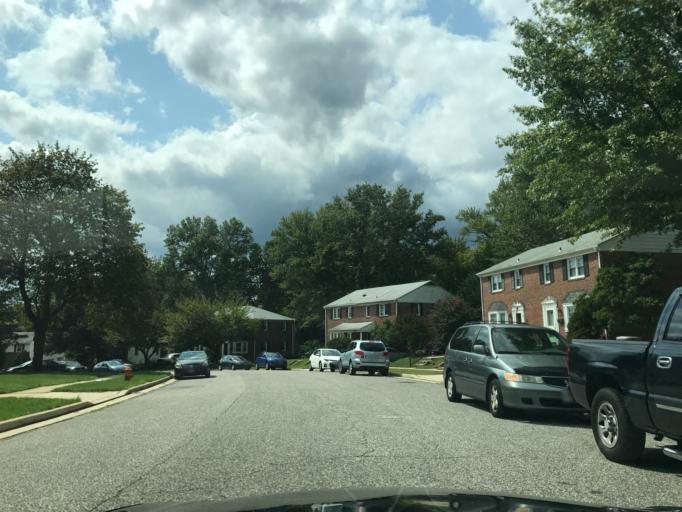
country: US
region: Maryland
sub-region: Baltimore County
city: Lutherville
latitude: 39.4191
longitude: -76.6394
